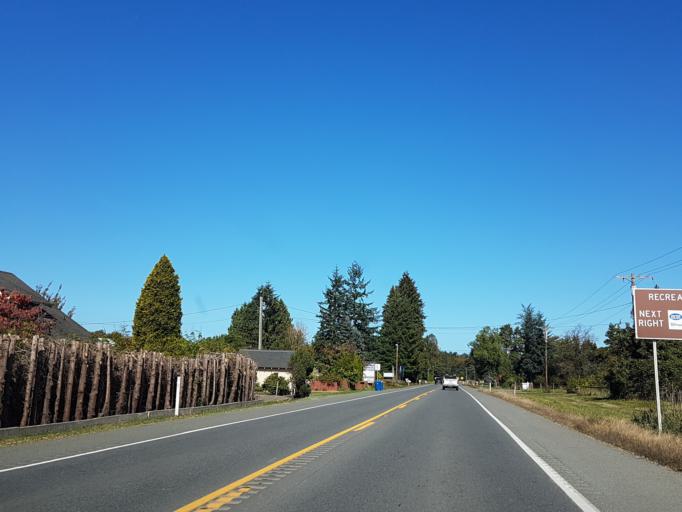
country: US
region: Washington
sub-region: Snohomish County
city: Monroe
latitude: 47.8364
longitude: -121.9693
